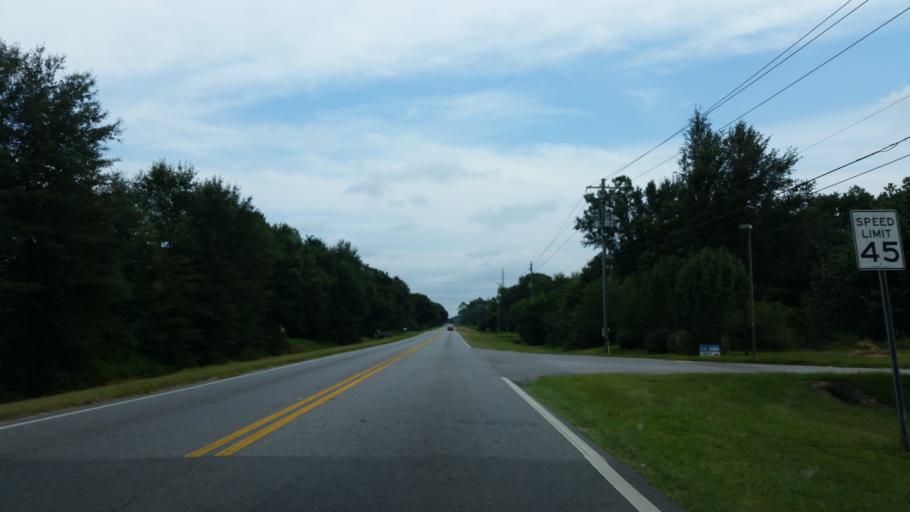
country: US
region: Florida
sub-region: Santa Rosa County
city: Wallace
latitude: 30.6421
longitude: -87.1796
